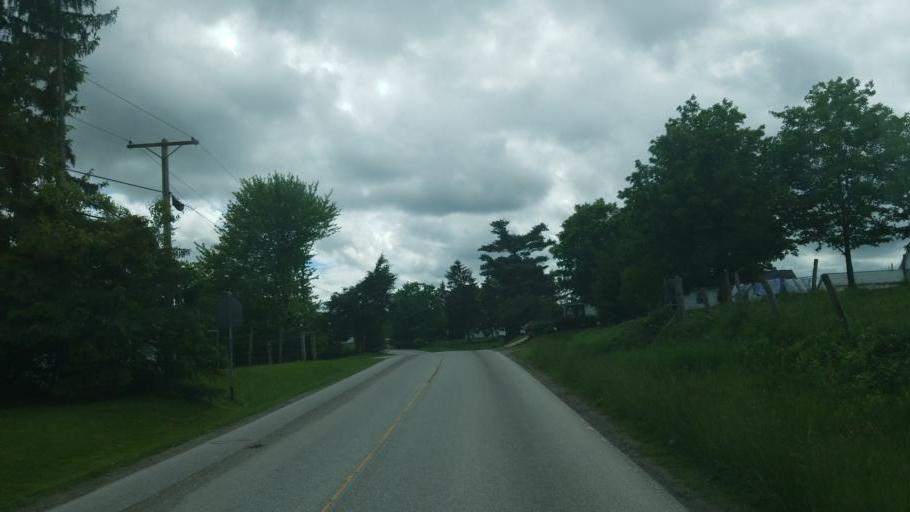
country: US
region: Ohio
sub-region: Geauga County
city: Middlefield
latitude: 41.4195
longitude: -81.0109
